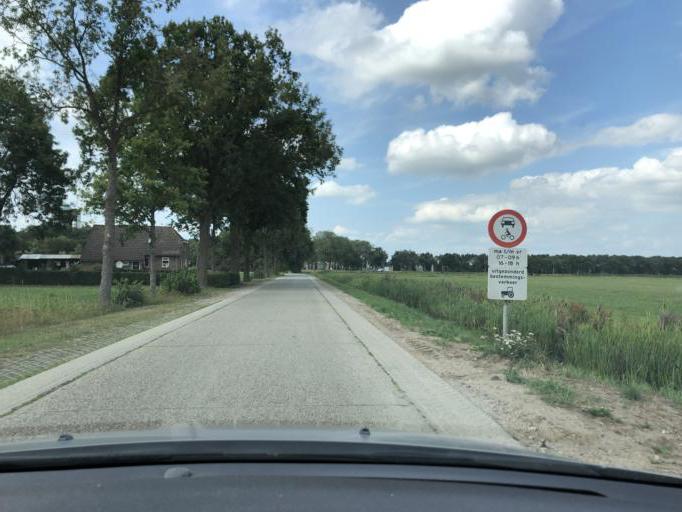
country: NL
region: Overijssel
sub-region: Gemeente Staphorst
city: Staphorst
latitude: 52.5800
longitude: 6.1956
